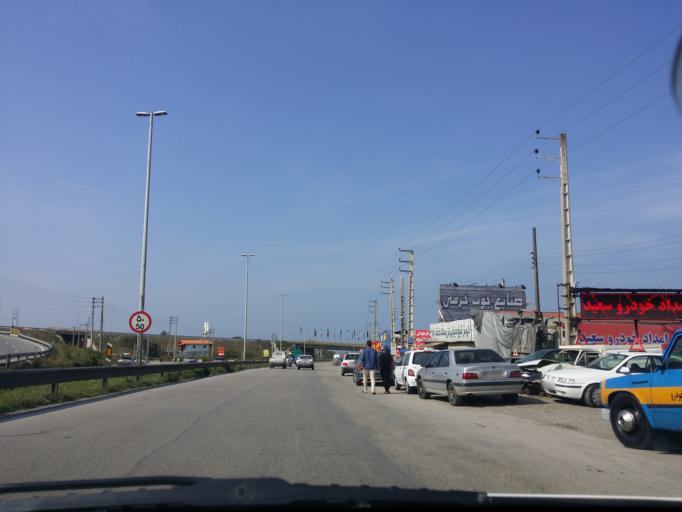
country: IR
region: Mazandaran
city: Chalus
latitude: 36.6499
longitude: 51.4076
